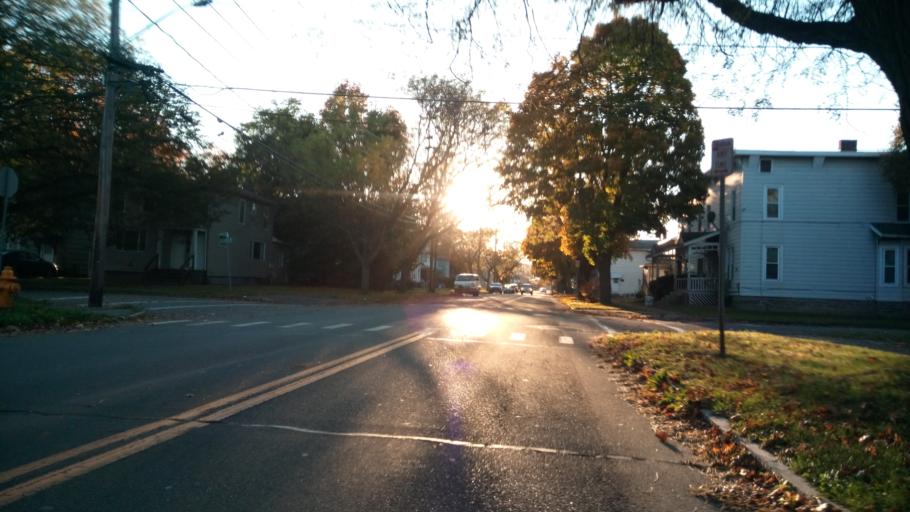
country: US
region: New York
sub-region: Chemung County
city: Elmira
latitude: 42.0833
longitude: -76.8068
